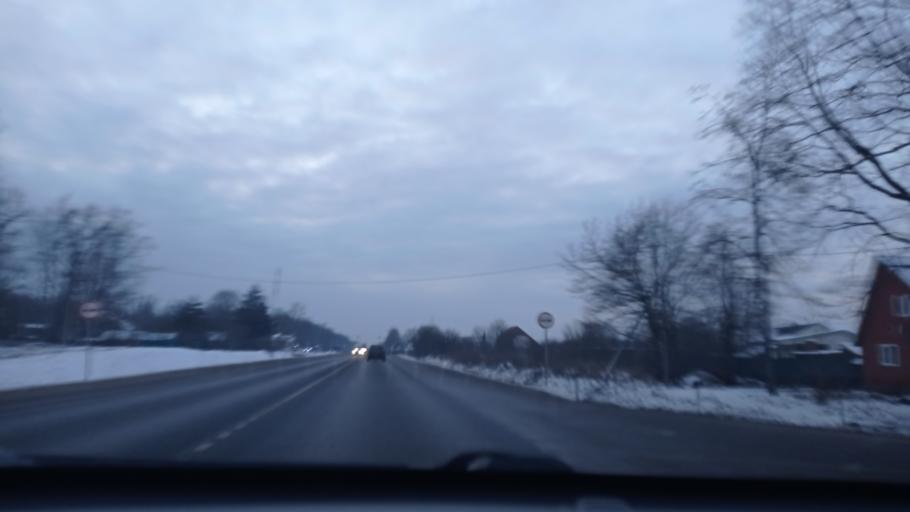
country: RU
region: Kaluga
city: Belousovo
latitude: 55.1150
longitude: 36.7229
